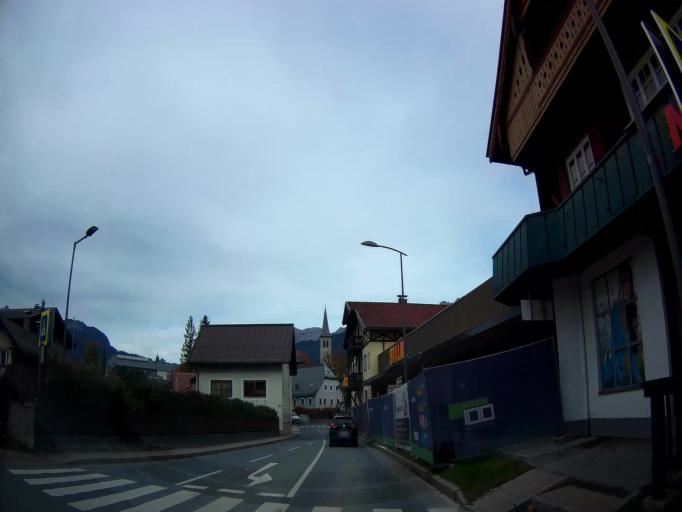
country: AT
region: Salzburg
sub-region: Politischer Bezirk Zell am See
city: Saalfelden am Steinernen Meer
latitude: 47.4247
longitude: 12.8483
